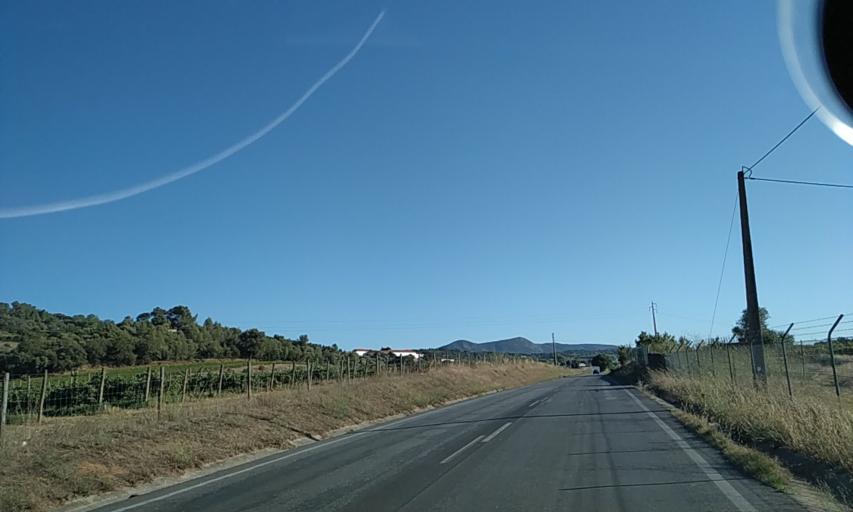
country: PT
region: Setubal
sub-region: Palmela
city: Quinta do Anjo
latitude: 38.5459
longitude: -8.9838
